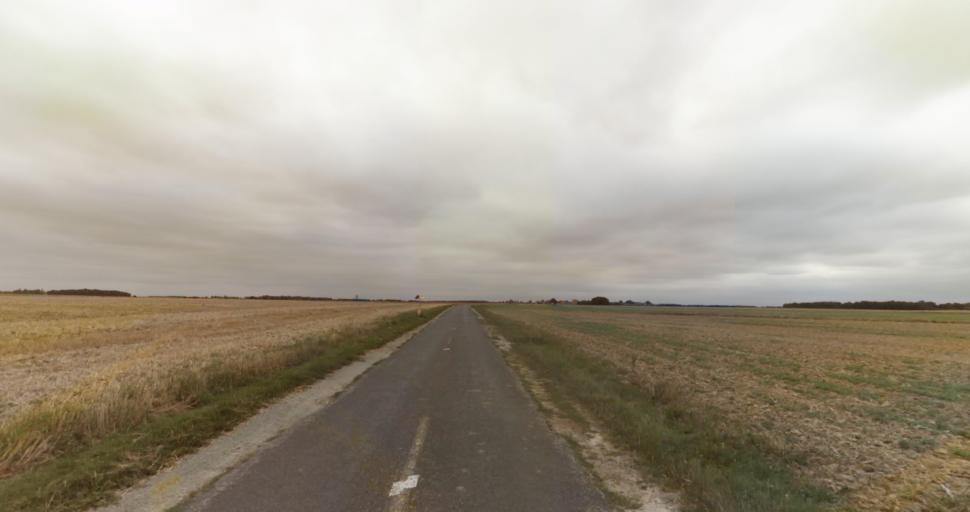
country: FR
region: Haute-Normandie
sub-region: Departement de l'Eure
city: La Couture-Boussey
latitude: 48.9186
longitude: 1.3360
